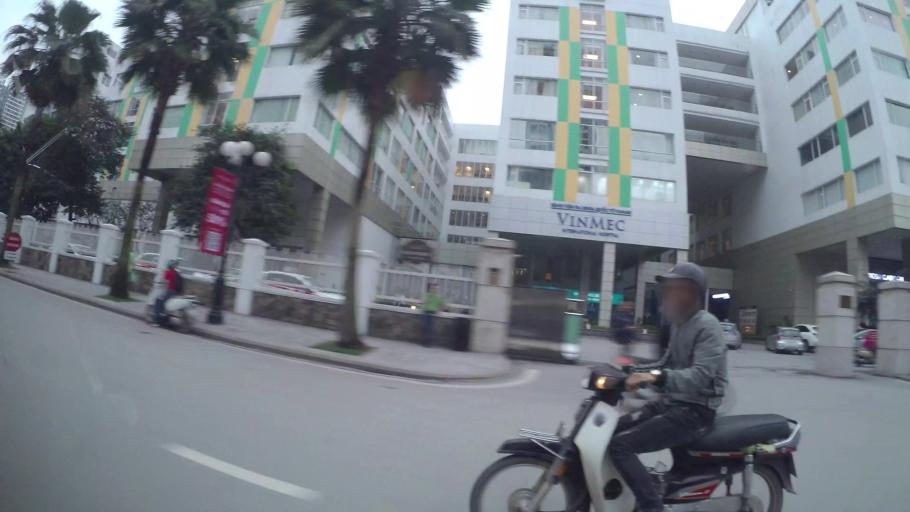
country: VN
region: Ha Noi
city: Hai BaTrung
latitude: 20.9963
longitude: 105.8675
